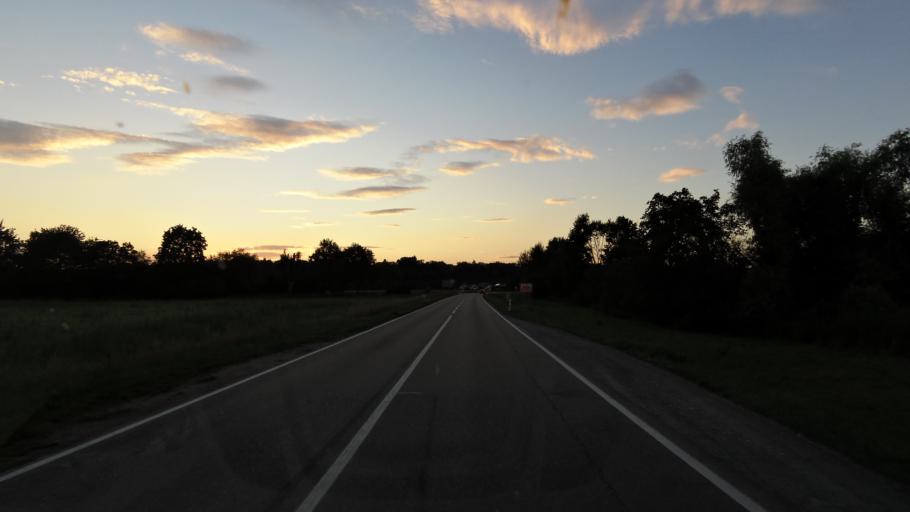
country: DE
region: Bavaria
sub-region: Upper Bavaria
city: Kraiburg am Inn
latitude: 48.1945
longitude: 12.4249
